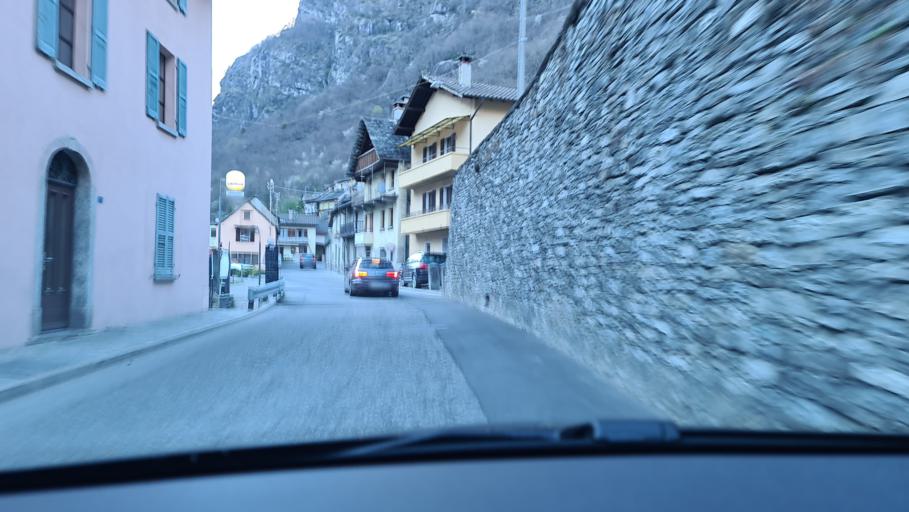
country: CH
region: Ticino
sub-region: Vallemaggia District
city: Cevio
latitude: 46.3444
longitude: 8.6068
